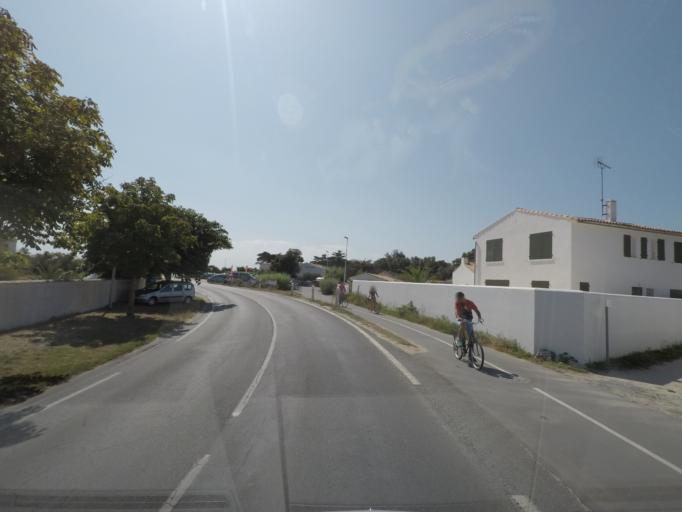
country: FR
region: Poitou-Charentes
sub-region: Departement de la Charente-Maritime
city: Ars-en-Re
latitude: 46.2015
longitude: -1.4862
